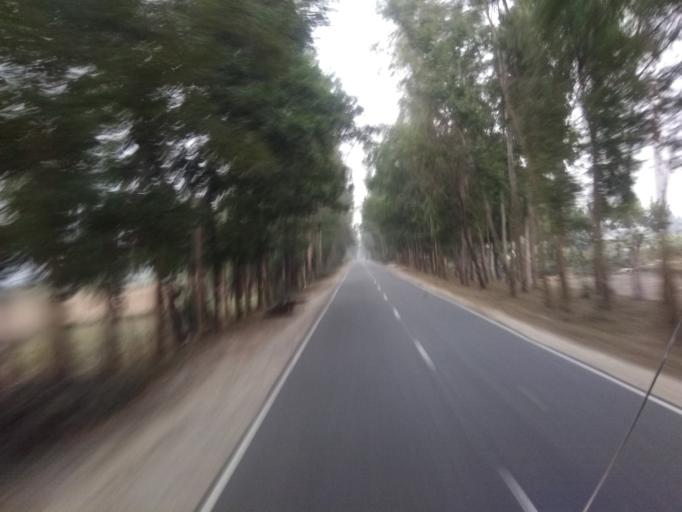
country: BD
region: Rajshahi
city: Bogra
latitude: 24.6666
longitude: 89.2735
